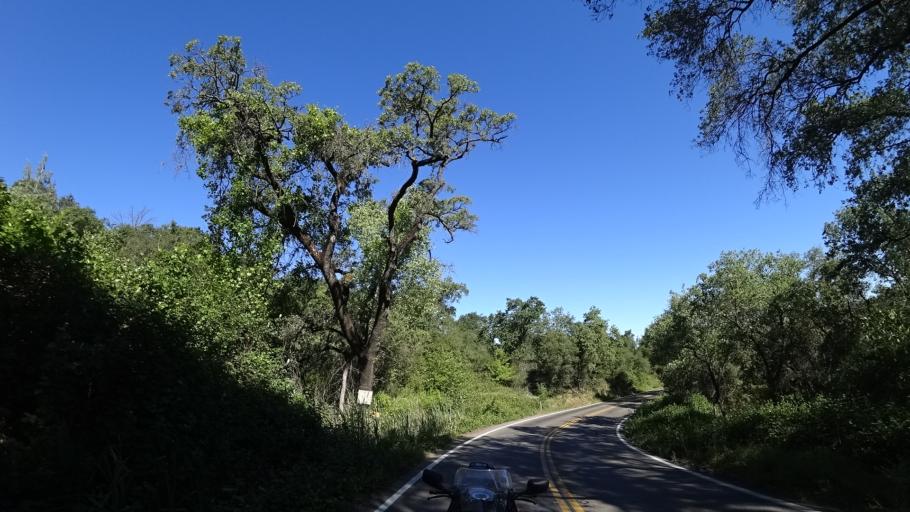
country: US
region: California
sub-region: Placer County
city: Newcastle
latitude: 38.8799
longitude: -121.1719
